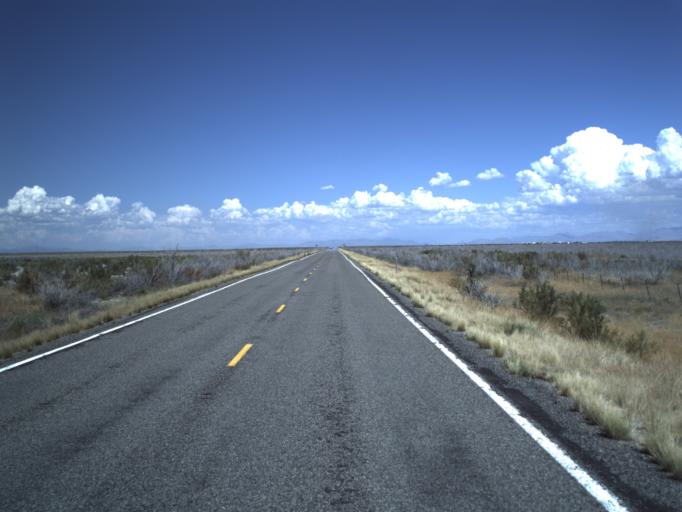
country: US
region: Utah
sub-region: Millard County
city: Delta
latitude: 39.2776
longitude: -112.8506
